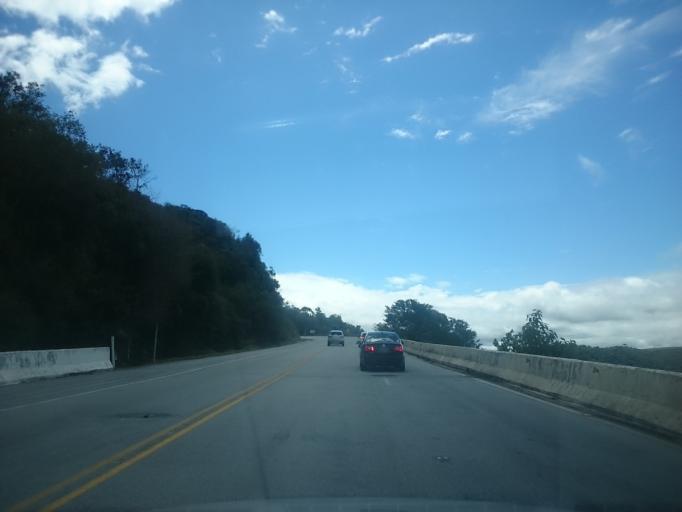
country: BR
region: Santa Catarina
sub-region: Anitapolis
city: Anitapolis
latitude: -27.6825
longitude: -49.1087
